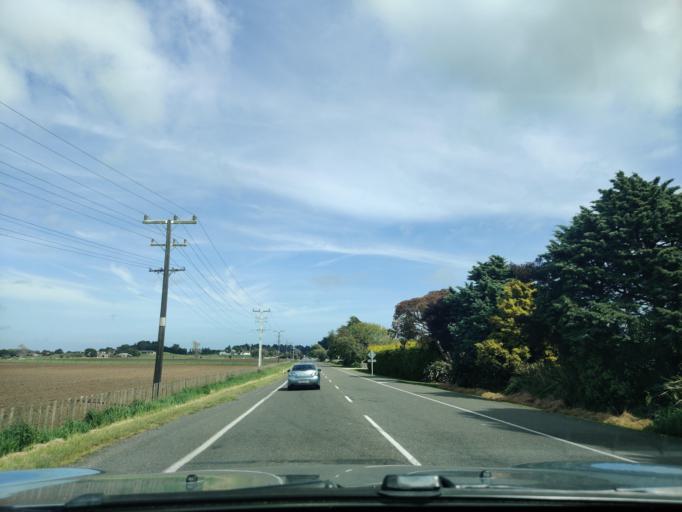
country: NZ
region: Manawatu-Wanganui
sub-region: Wanganui District
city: Wanganui
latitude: -39.8897
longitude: 175.0069
